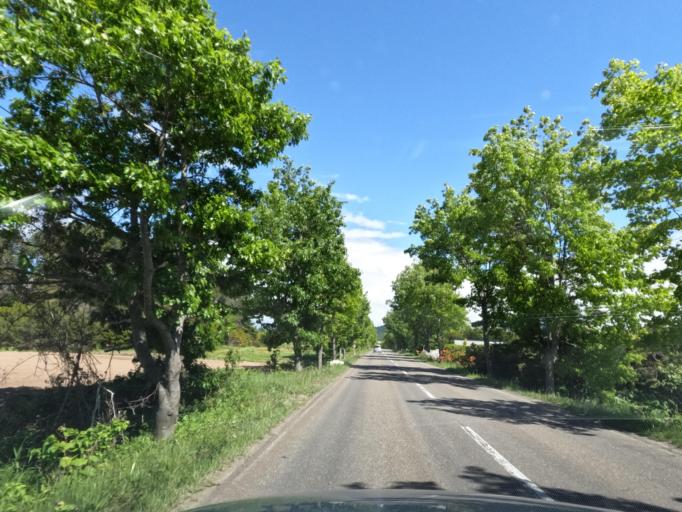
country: JP
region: Hokkaido
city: Kitahiroshima
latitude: 43.0212
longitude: 141.7095
